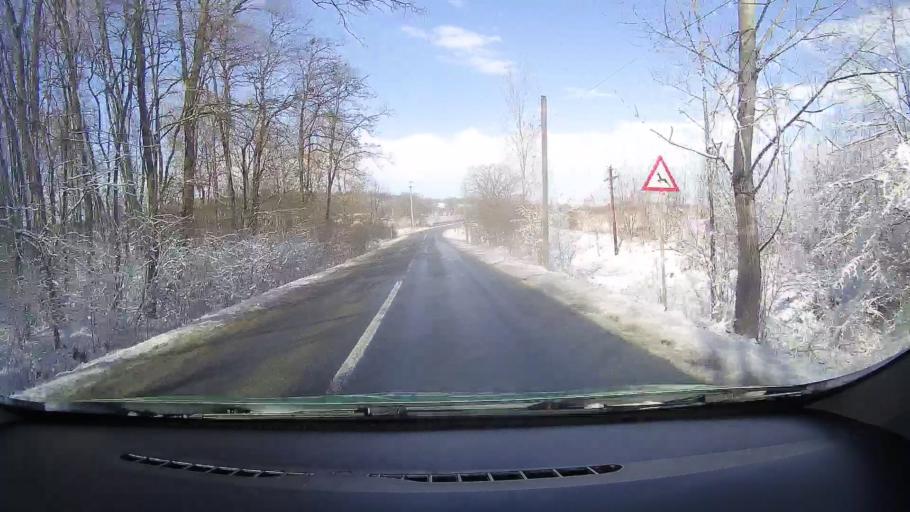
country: RO
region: Sibiu
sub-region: Comuna Nocrich
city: Nocrich
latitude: 45.8698
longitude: 24.4518
